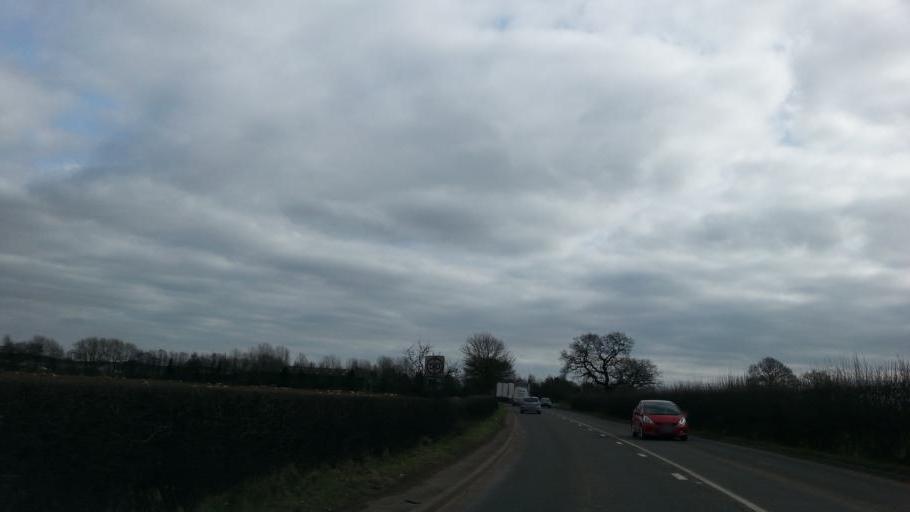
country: GB
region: England
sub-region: Staffordshire
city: Colwich
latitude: 52.8363
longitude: -2.0318
